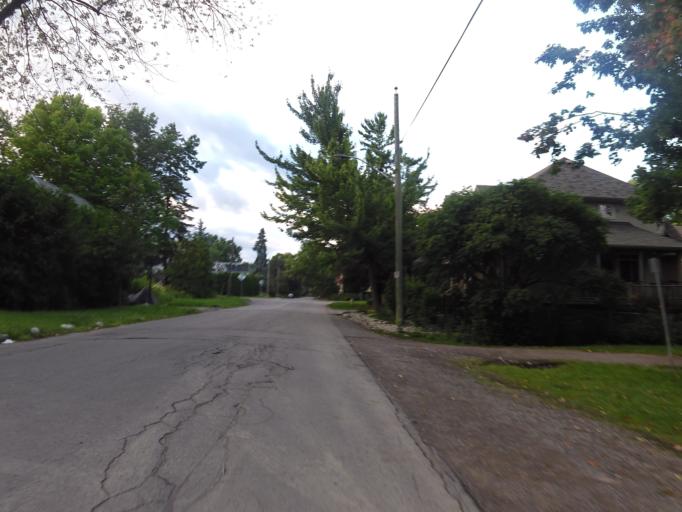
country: CA
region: Ontario
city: Ottawa
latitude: 45.3837
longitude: -75.7548
